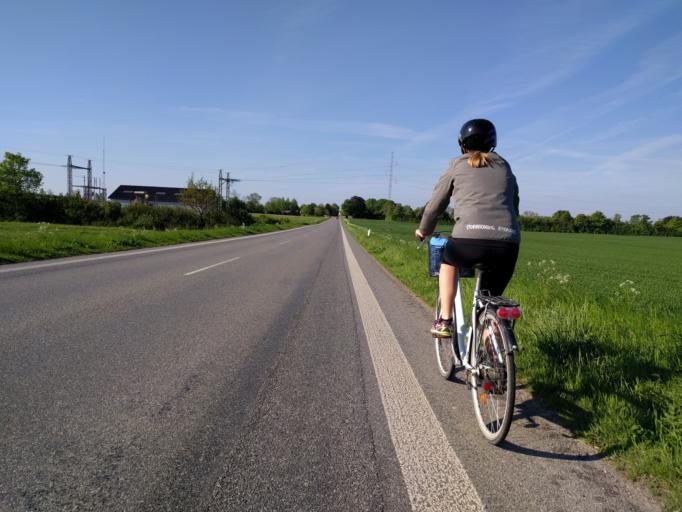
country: DK
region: Zealand
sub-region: Guldborgsund Kommune
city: Stubbekobing
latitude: 54.8696
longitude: 12.0234
